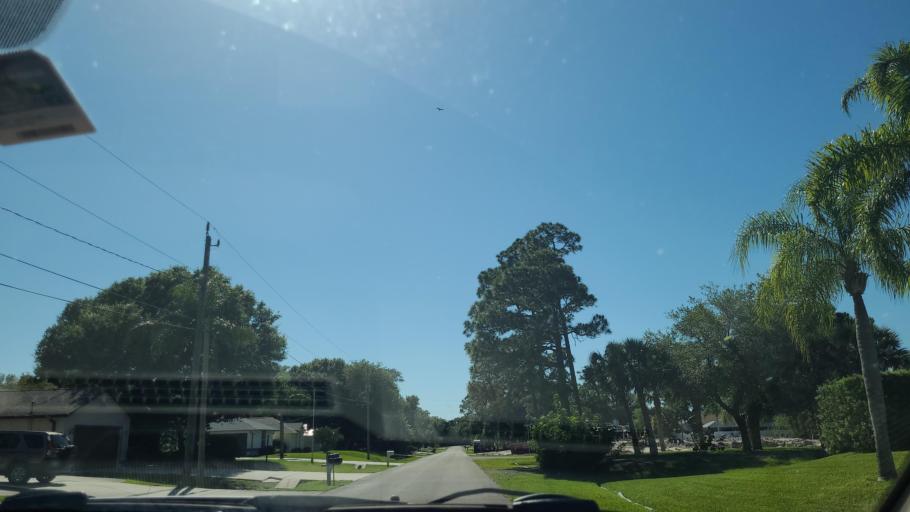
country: US
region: Florida
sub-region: Indian River County
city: Sebastian
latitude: 27.7602
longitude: -80.4959
